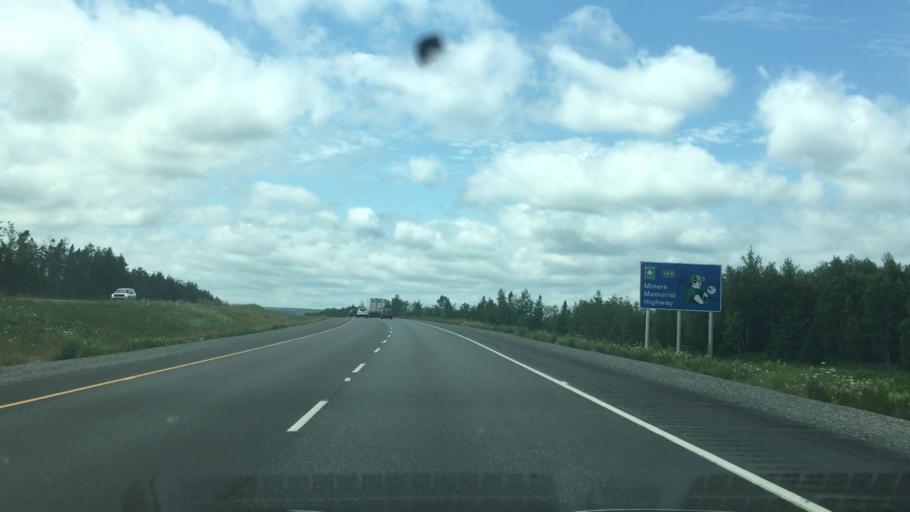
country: CA
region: Nova Scotia
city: Springhill
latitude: 45.7056
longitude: -63.9715
